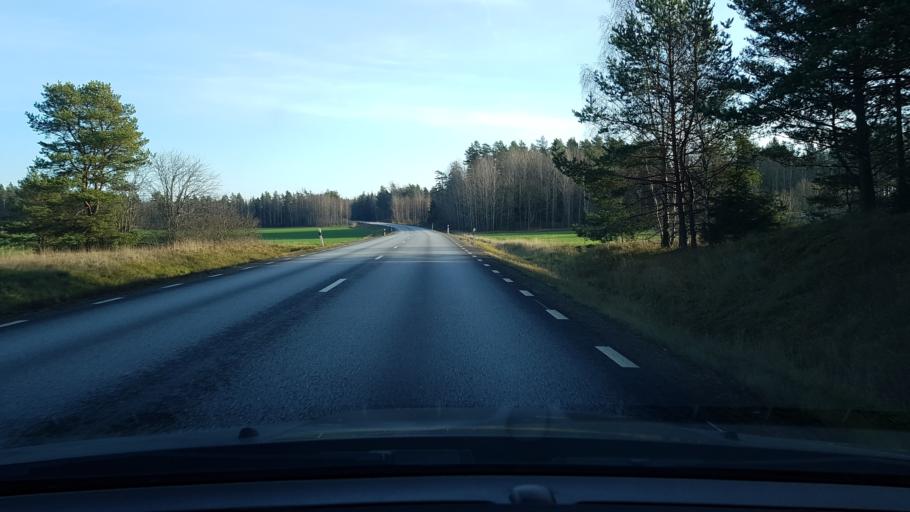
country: SE
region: Stockholm
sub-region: Vallentuna Kommun
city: Vallentuna
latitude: 59.7475
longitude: 18.0762
